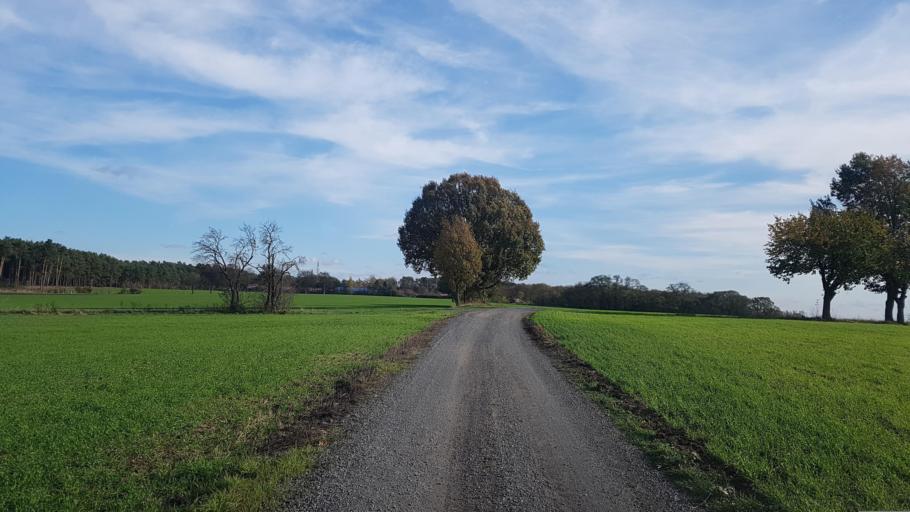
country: DE
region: Brandenburg
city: Schlieben
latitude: 51.7375
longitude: 13.3711
